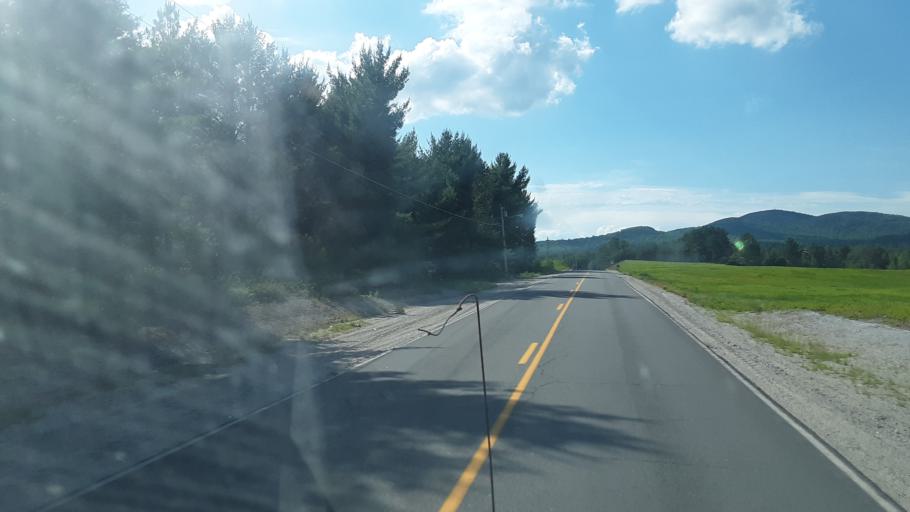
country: US
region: Maine
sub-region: Washington County
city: Cherryfield
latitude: 44.8258
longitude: -68.0794
